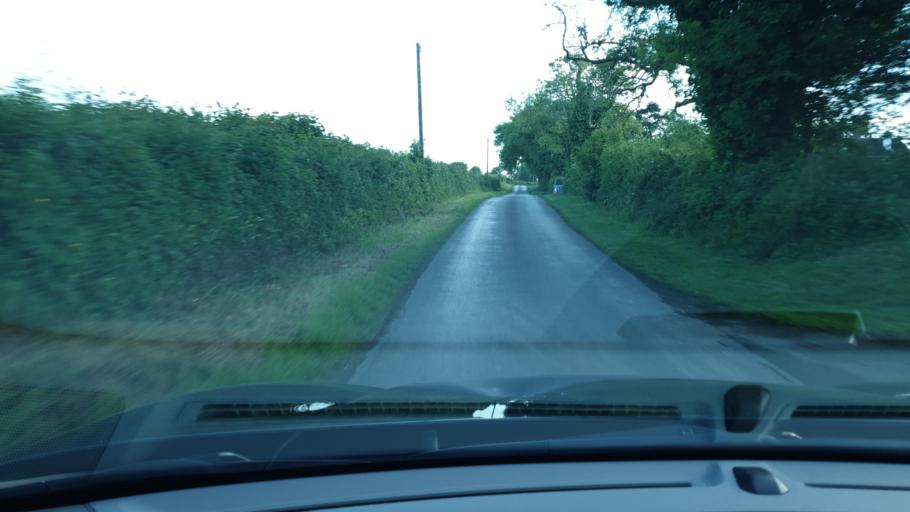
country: IE
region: Leinster
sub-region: An Mhi
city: Ashbourne
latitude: 53.4828
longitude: -6.3495
